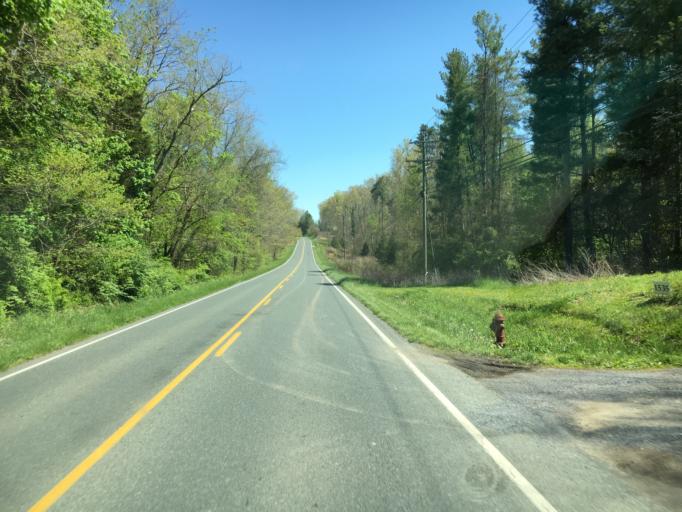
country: US
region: Virginia
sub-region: Augusta County
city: Crimora
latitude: 38.1430
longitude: -78.8425
